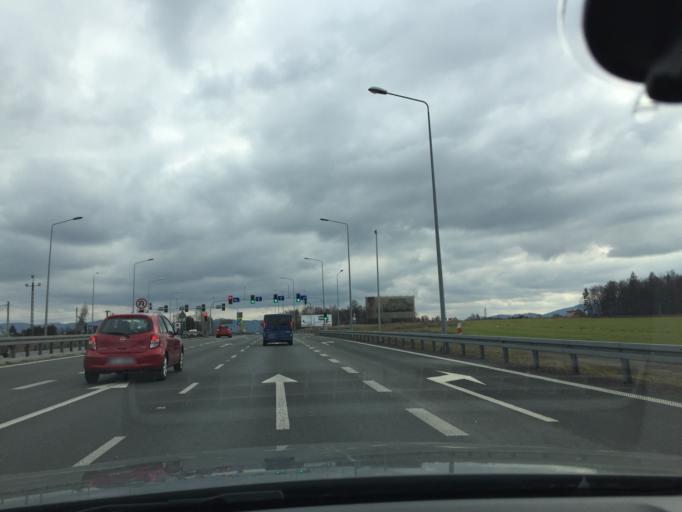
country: PL
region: Silesian Voivodeship
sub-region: Powiat bielski
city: Mazancowice
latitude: 49.8724
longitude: 19.0038
